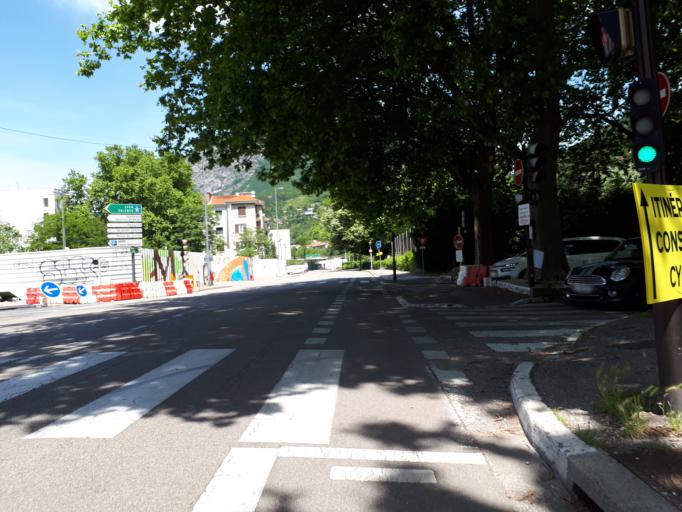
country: FR
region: Rhone-Alpes
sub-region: Departement de l'Isere
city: Saint-Martin-le-Vinoux
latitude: 45.1995
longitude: 5.7142
